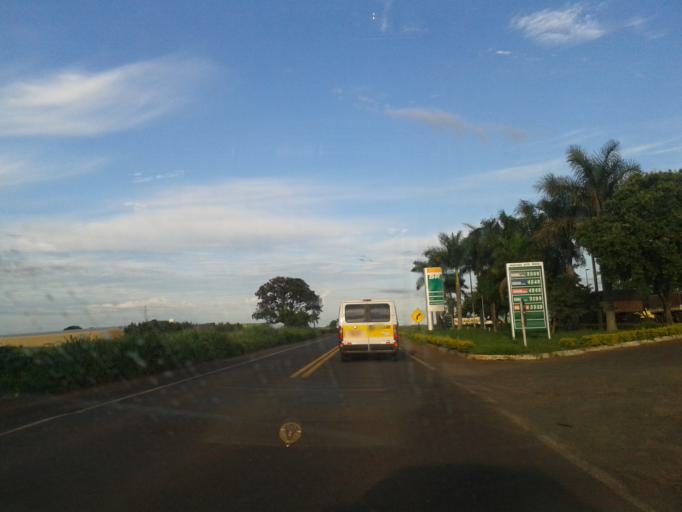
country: BR
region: Minas Gerais
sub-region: Araguari
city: Araguari
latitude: -18.6410
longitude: -48.2203
